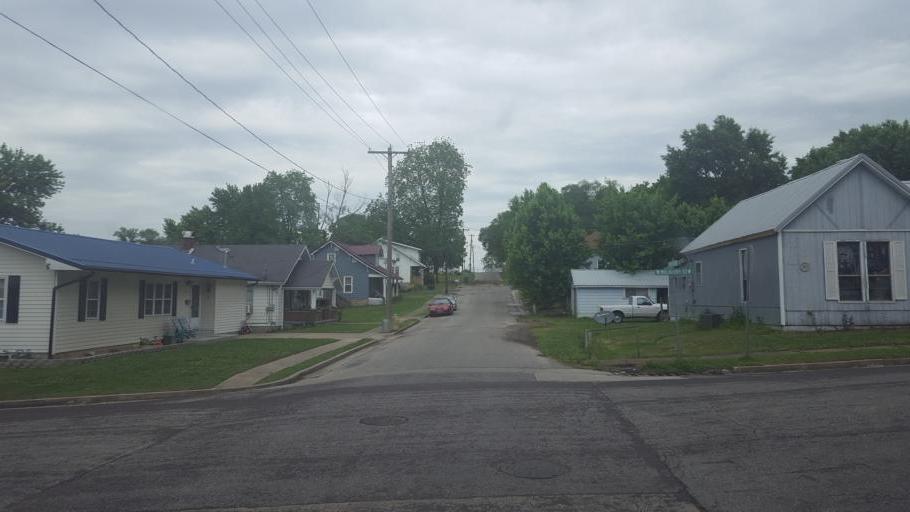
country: US
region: Missouri
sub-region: Moniteau County
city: California
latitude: 38.6378
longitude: -92.5676
